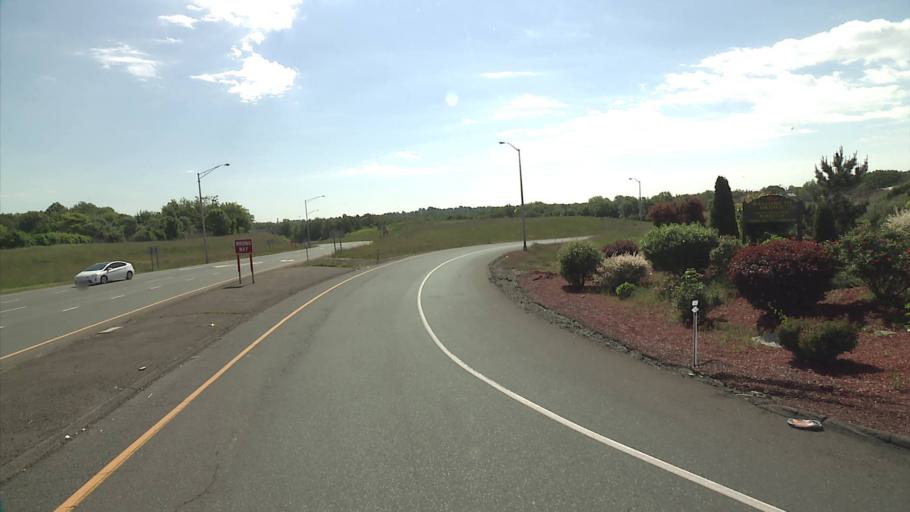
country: US
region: Connecticut
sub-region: New Haven County
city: Woodmont
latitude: 41.2553
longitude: -72.9999
